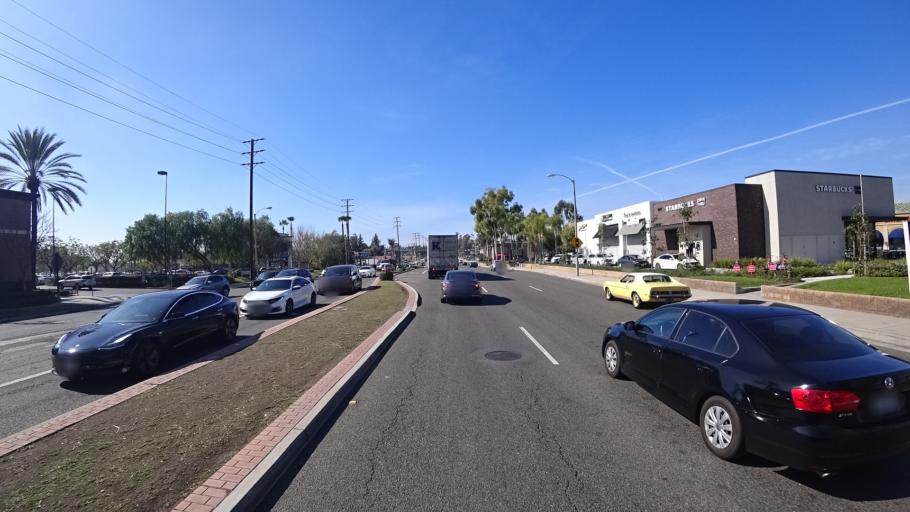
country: US
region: California
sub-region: Los Angeles County
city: East La Mirada
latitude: 33.9174
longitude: -117.9660
